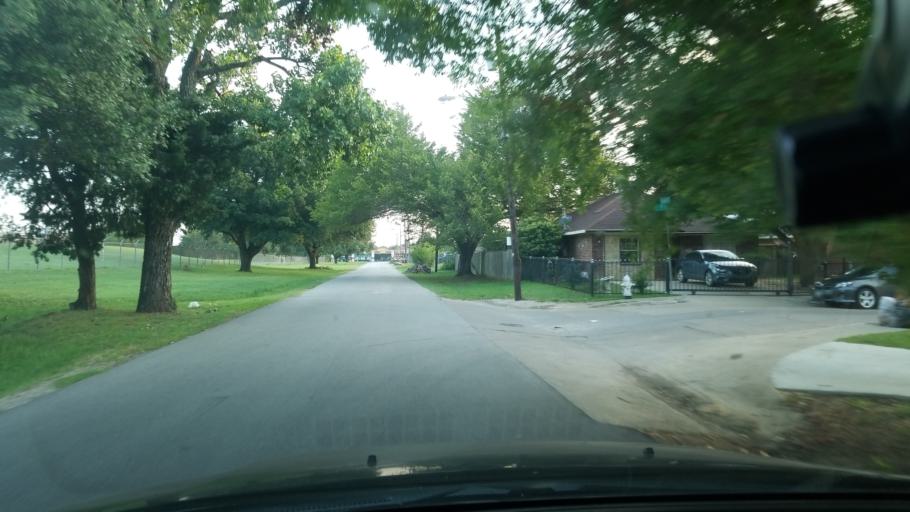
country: US
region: Texas
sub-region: Dallas County
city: Balch Springs
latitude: 32.7316
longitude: -96.6519
